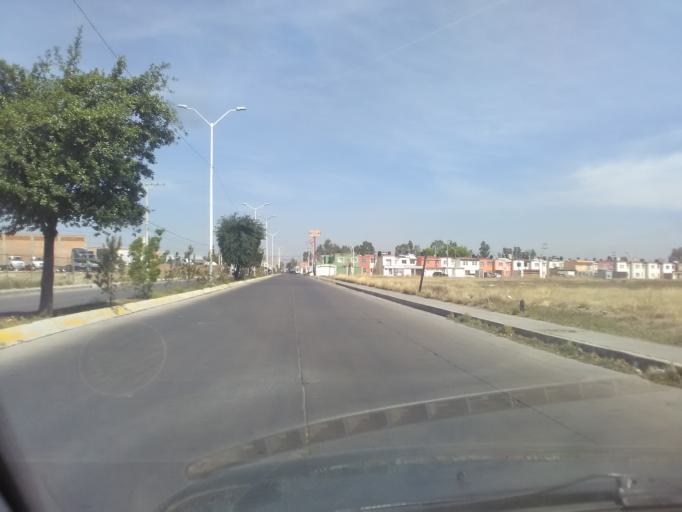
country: MX
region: Durango
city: Victoria de Durango
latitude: 24.0483
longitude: -104.6246
